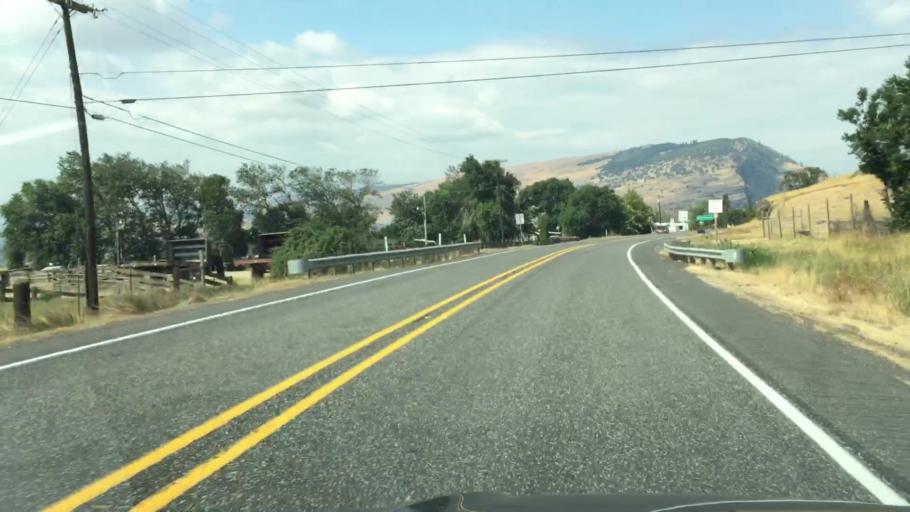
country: US
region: Washington
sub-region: Klickitat County
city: Dallesport
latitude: 45.6484
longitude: -121.1794
